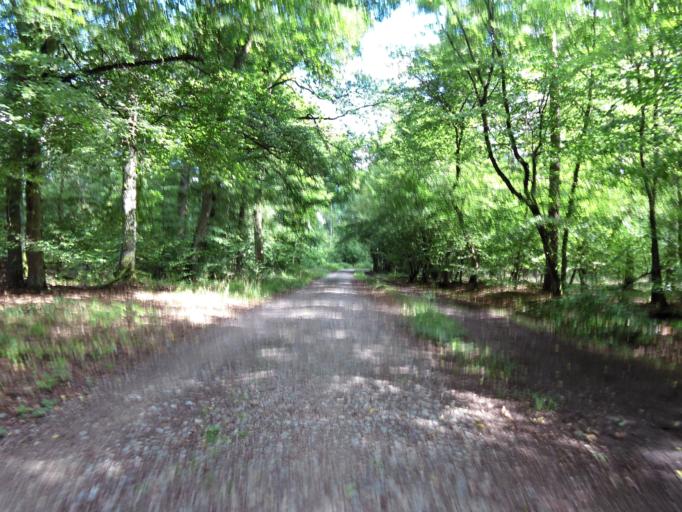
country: DE
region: Hesse
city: Lorsch
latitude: 49.6316
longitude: 8.5660
